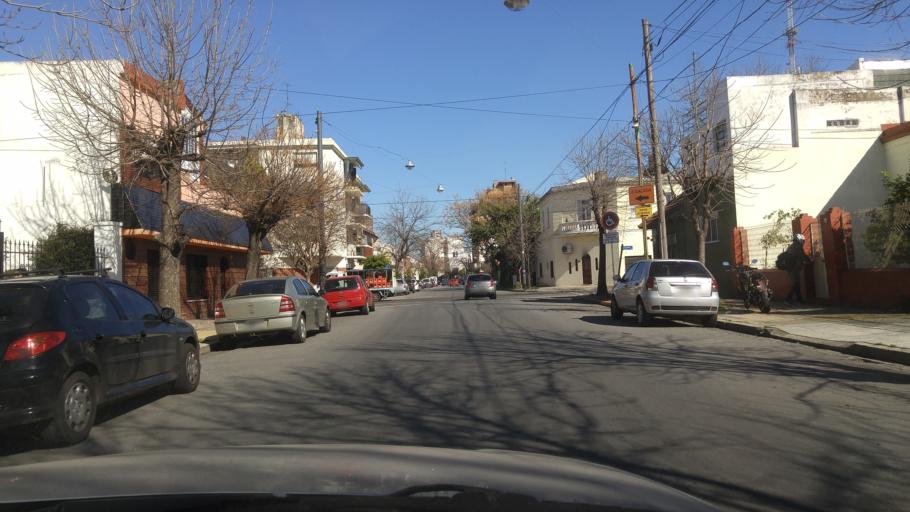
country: AR
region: Buenos Aires F.D.
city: Villa Santa Rita
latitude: -34.6193
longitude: -58.4800
